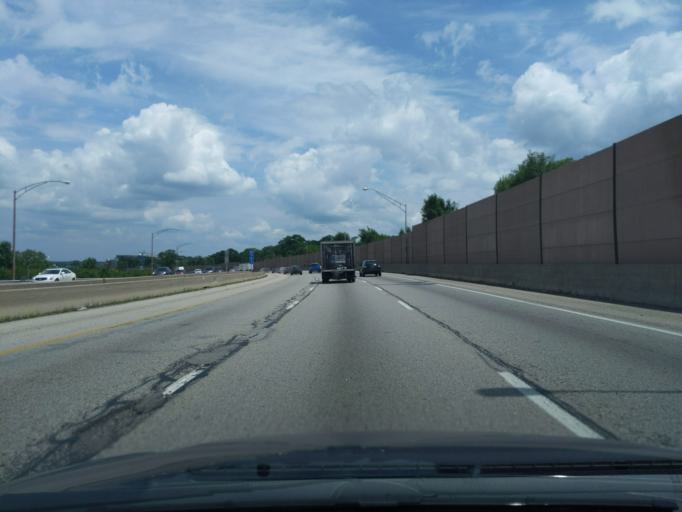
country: US
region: Ohio
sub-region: Hamilton County
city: Madeira
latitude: 39.1949
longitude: -84.3794
